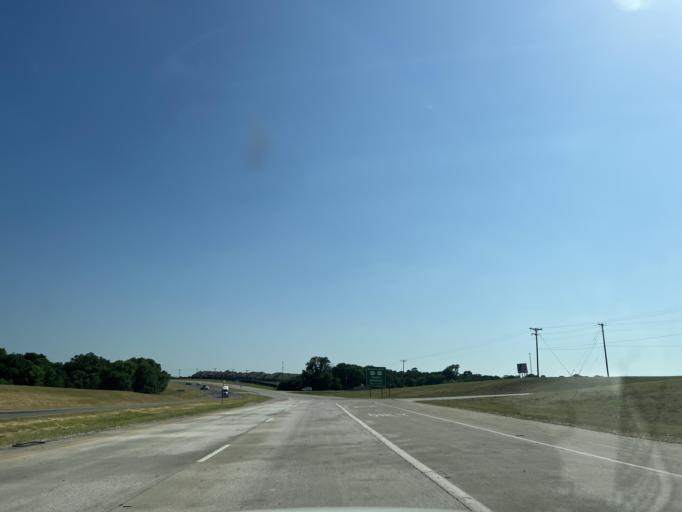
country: US
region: Texas
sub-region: Washington County
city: Brenham
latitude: 30.1770
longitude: -96.4227
